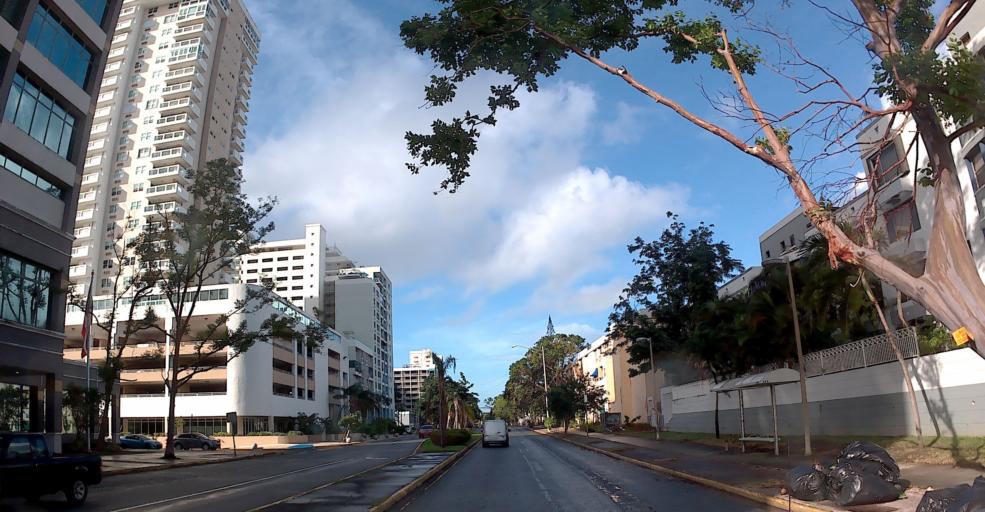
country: PR
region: Catano
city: Catano
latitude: 18.4289
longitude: -66.0631
